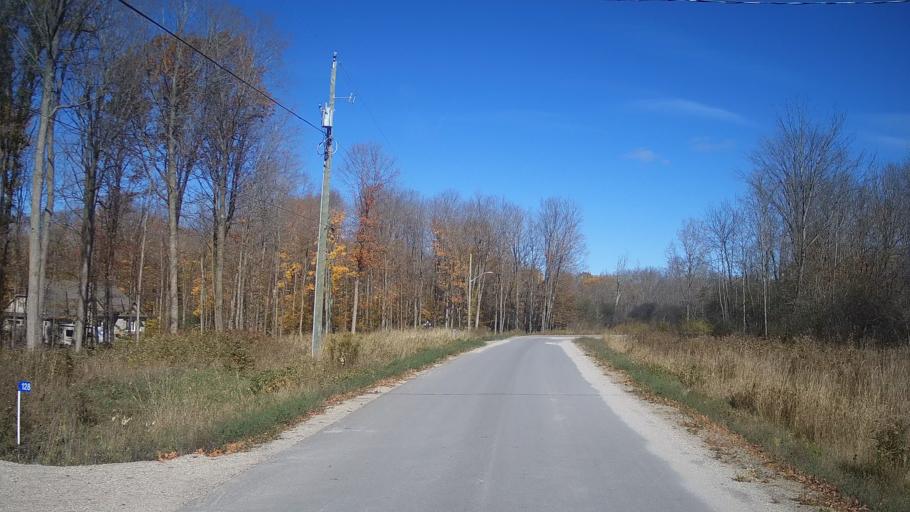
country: CA
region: Ontario
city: Perth
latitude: 44.8829
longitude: -76.2932
